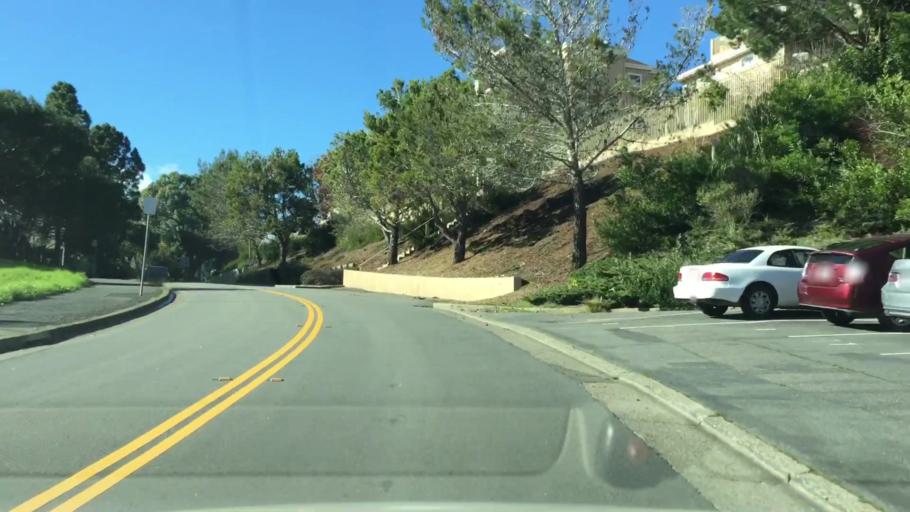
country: US
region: California
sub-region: Marin County
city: Strawberry
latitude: 37.8936
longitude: -122.5191
